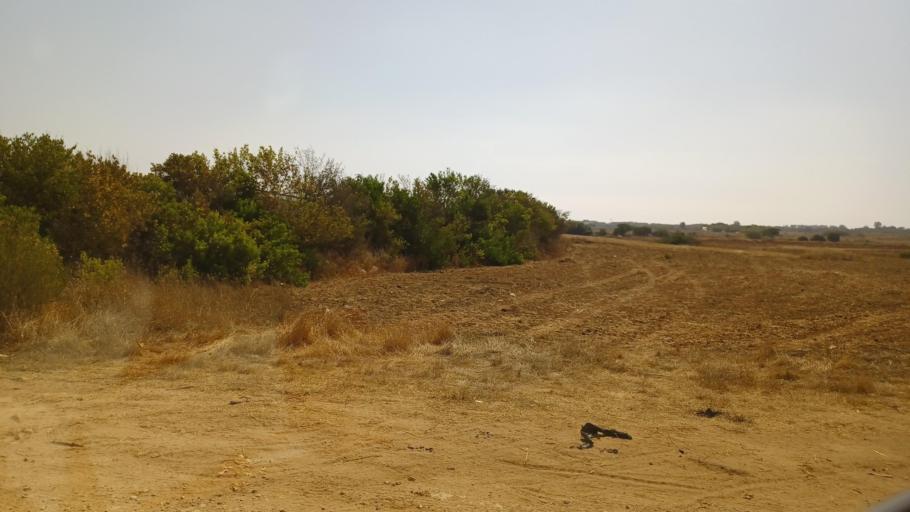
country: CY
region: Ammochostos
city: Paralimni
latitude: 35.0655
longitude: 33.9883
